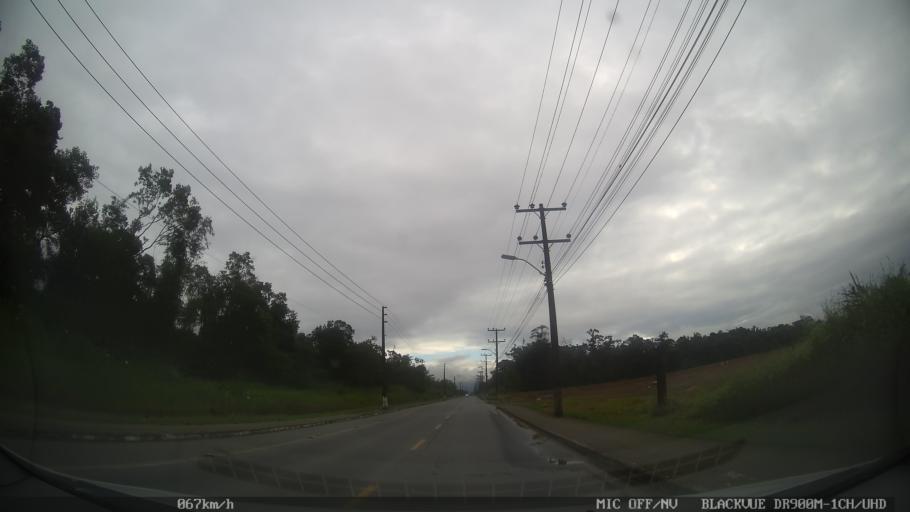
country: BR
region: Santa Catarina
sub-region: Joinville
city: Joinville
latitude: -26.0637
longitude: -48.8572
